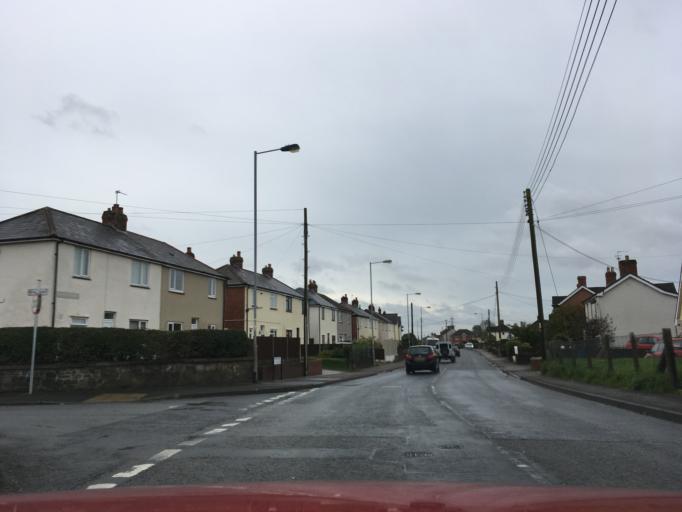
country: GB
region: Wales
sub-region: Monmouthshire
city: Caldicot
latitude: 51.5910
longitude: -2.7622
